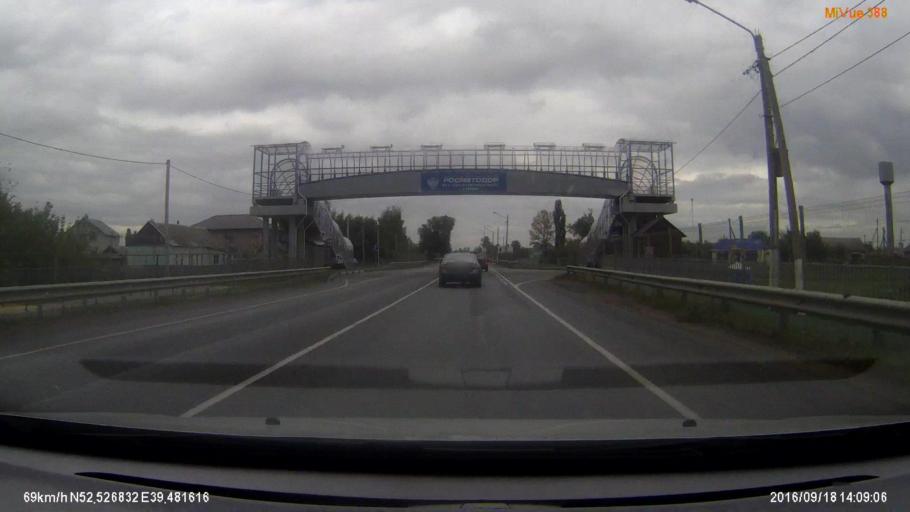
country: RU
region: Lipetsk
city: Syrskoye
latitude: 52.5913
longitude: 39.5258
